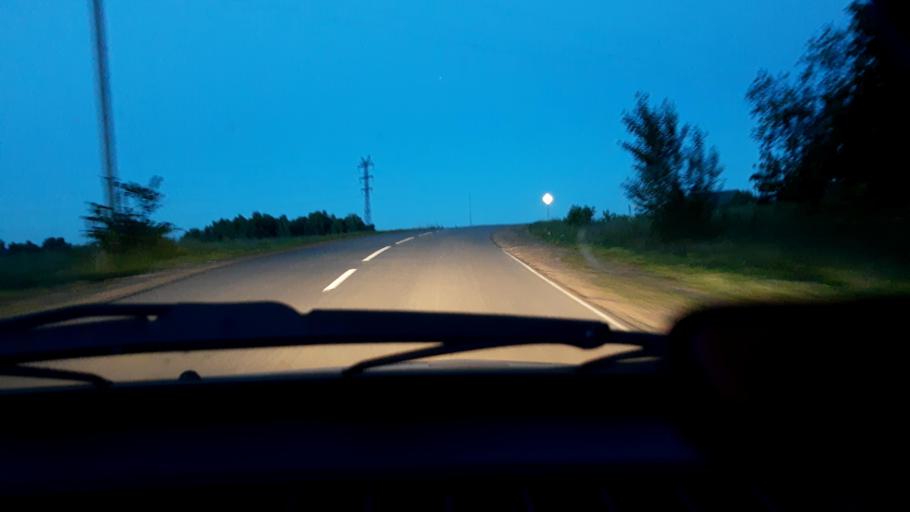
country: RU
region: Bashkortostan
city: Avdon
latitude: 54.6365
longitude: 55.6987
